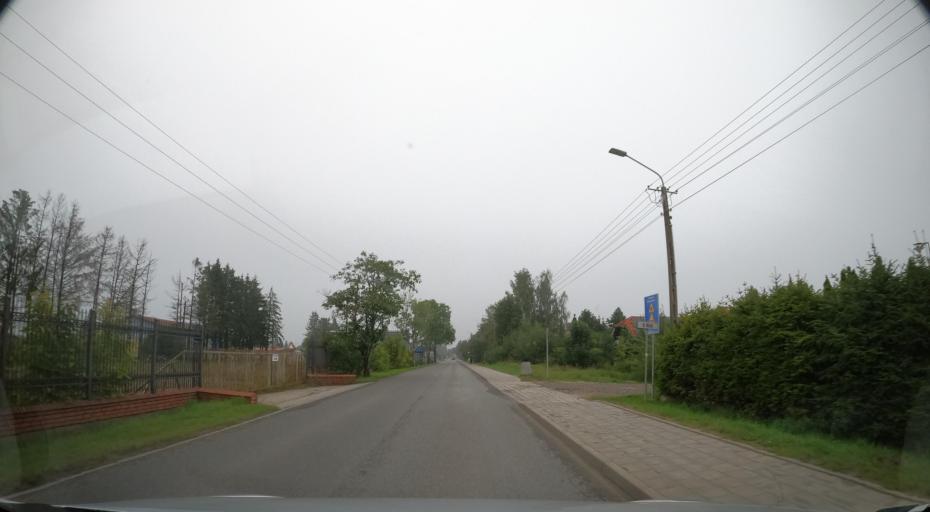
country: PL
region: Pomeranian Voivodeship
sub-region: Powiat kartuski
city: Chwaszczyno
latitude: 54.4223
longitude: 18.4545
